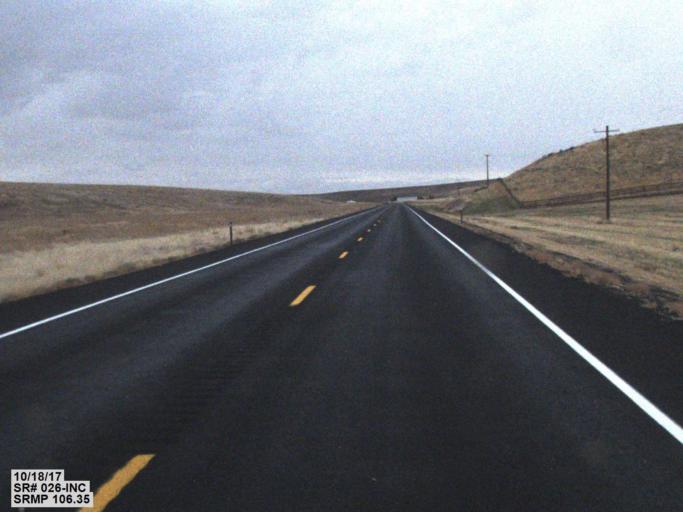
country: US
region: Washington
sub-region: Garfield County
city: Pomeroy
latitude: 46.7978
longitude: -117.8638
